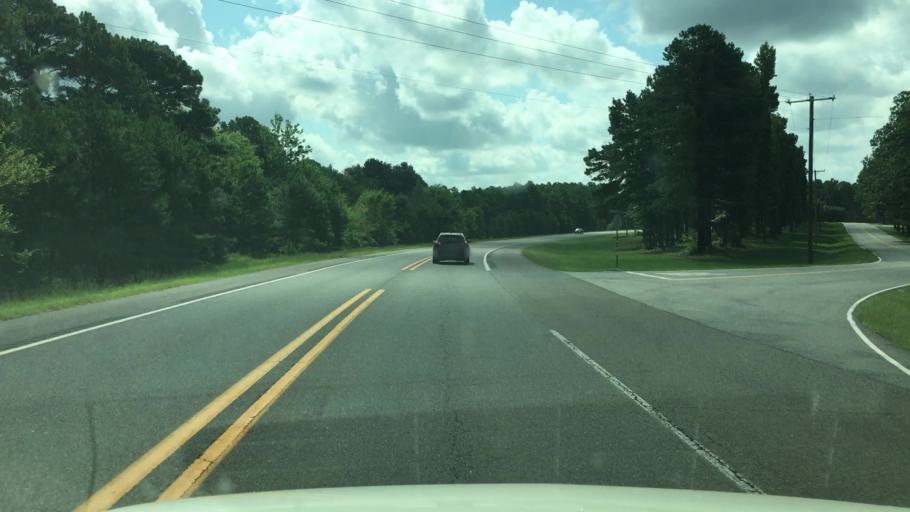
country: US
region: Arkansas
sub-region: Clark County
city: Arkadelphia
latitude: 34.2282
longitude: -93.0908
